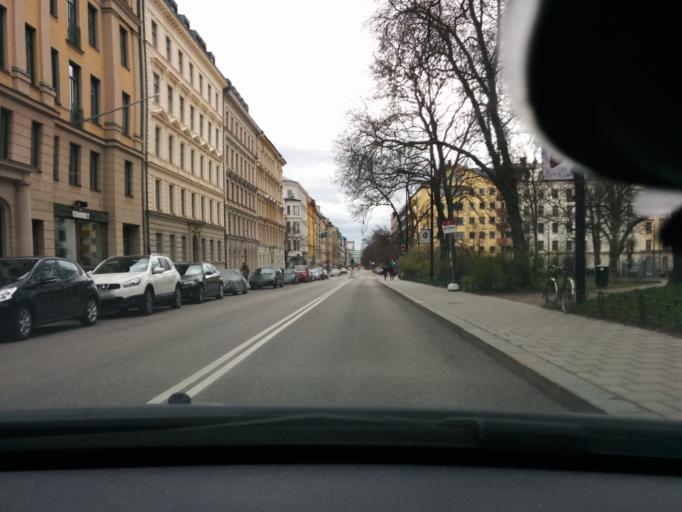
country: SE
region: Stockholm
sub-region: Stockholms Kommun
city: OEstermalm
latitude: 59.3429
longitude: 18.0782
